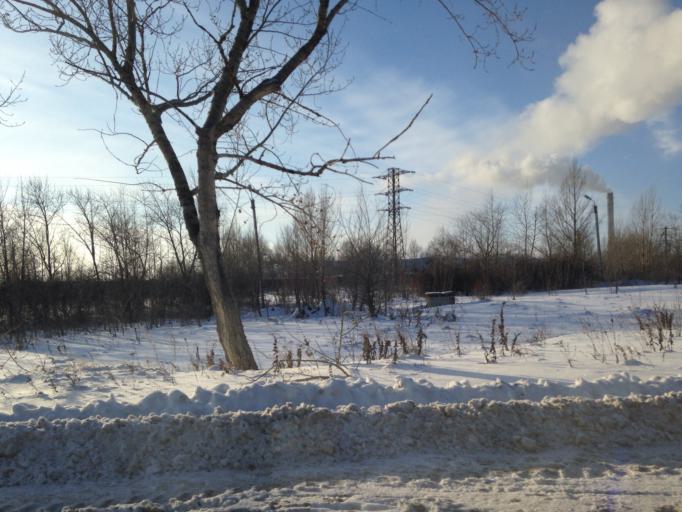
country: RU
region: Ulyanovsk
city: Novoul'yanovsk
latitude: 54.1559
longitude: 48.3690
